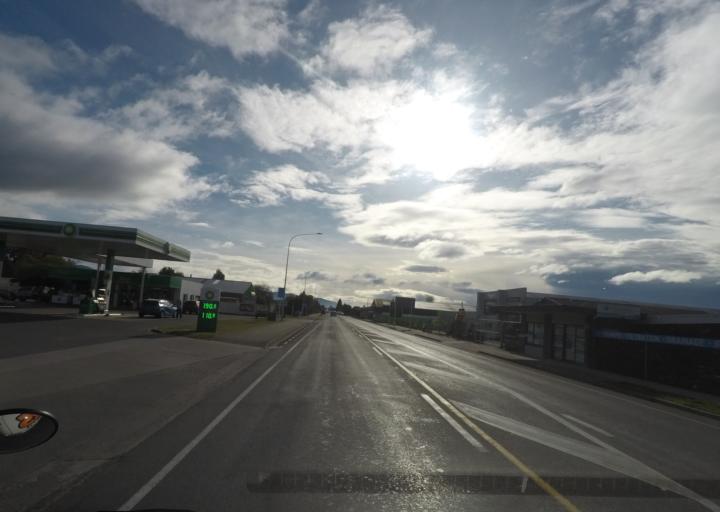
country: NZ
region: Tasman
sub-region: Tasman District
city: Motueka
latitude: -41.1240
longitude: 173.0104
